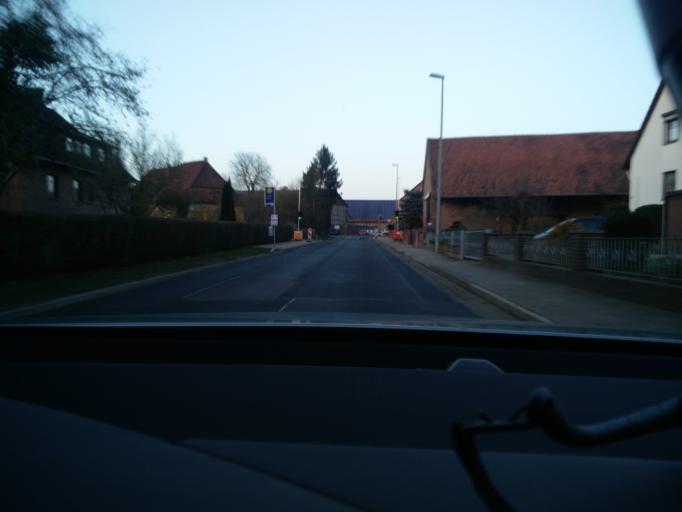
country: DE
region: Lower Saxony
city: Hohenhameln
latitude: 52.3175
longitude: 10.0486
